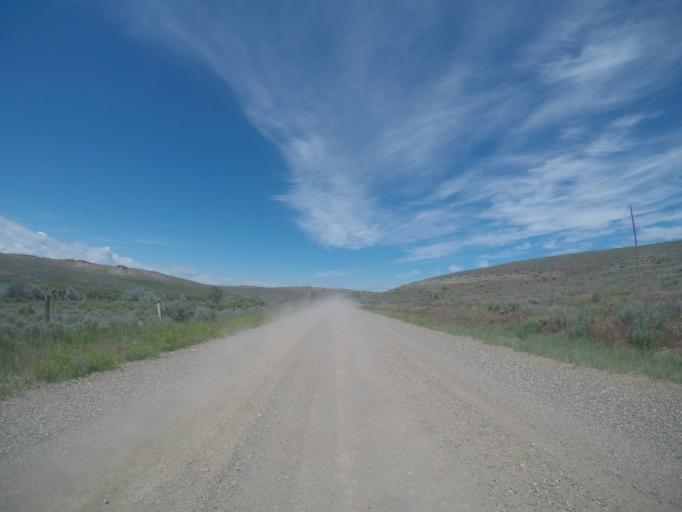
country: US
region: Montana
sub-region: Carbon County
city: Red Lodge
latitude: 45.2313
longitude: -108.8474
